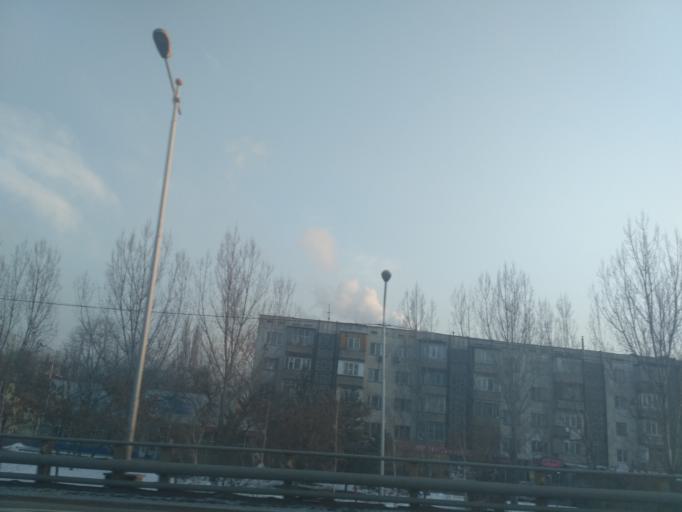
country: KZ
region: Almaty Qalasy
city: Almaty
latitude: 43.2469
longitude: 76.8404
